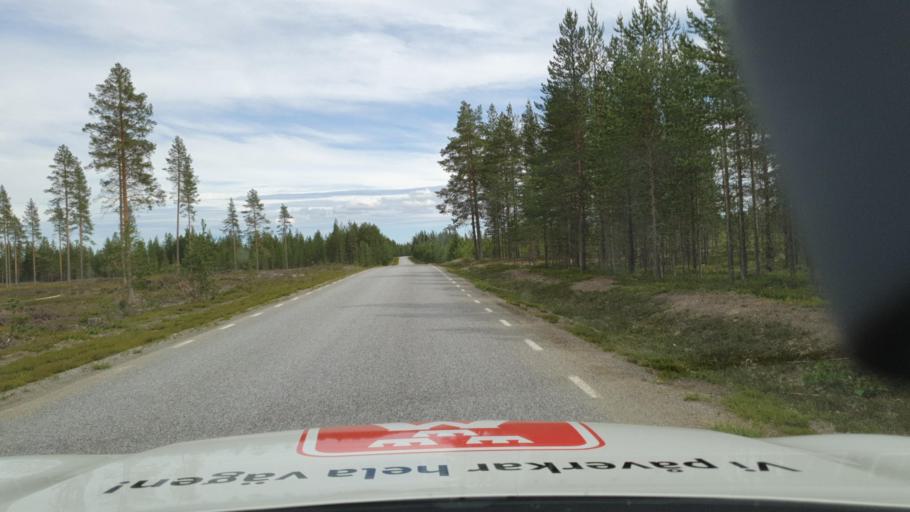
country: SE
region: Vaesterbotten
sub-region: Skelleftea Kommun
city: Burtraesk
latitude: 64.5037
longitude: 20.8210
